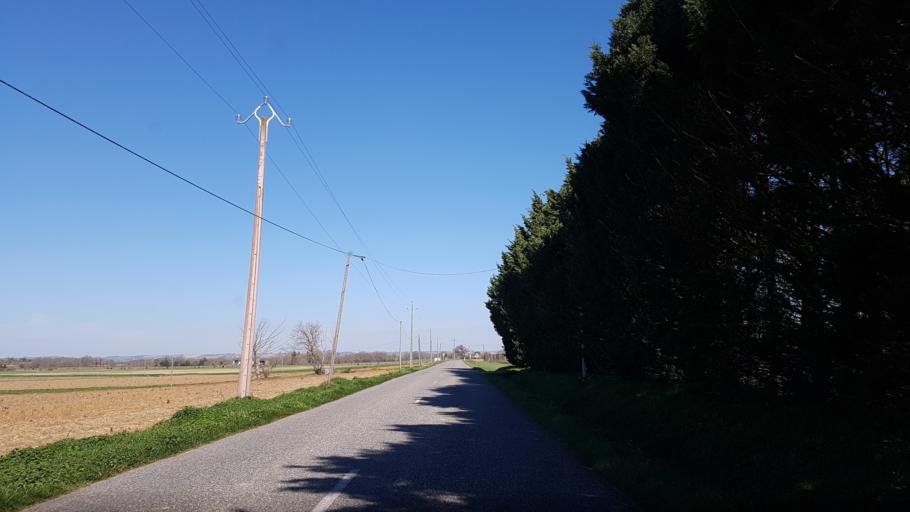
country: FR
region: Languedoc-Roussillon
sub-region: Departement de l'Aude
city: Belpech
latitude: 43.1782
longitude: 1.7112
